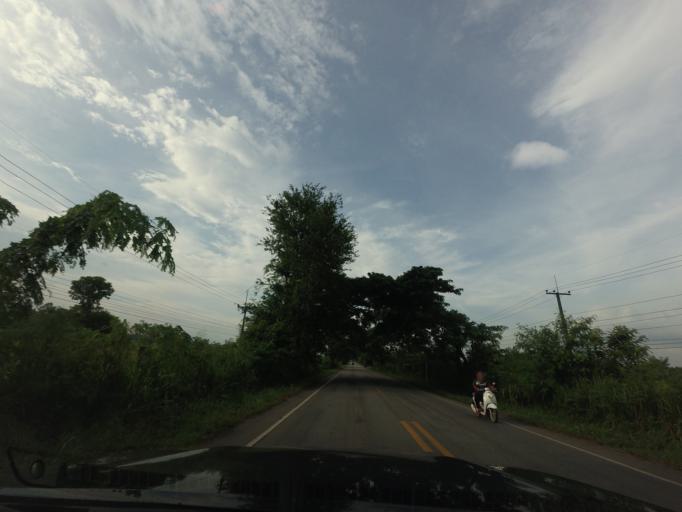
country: TH
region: Changwat Udon Thani
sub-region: Amphoe Ban Phue
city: Ban Phue
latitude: 17.7576
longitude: 102.3978
